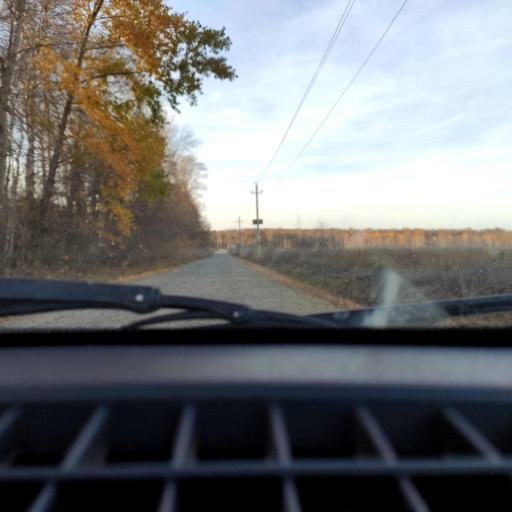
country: RU
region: Bashkortostan
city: Avdon
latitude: 54.6300
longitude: 55.7344
